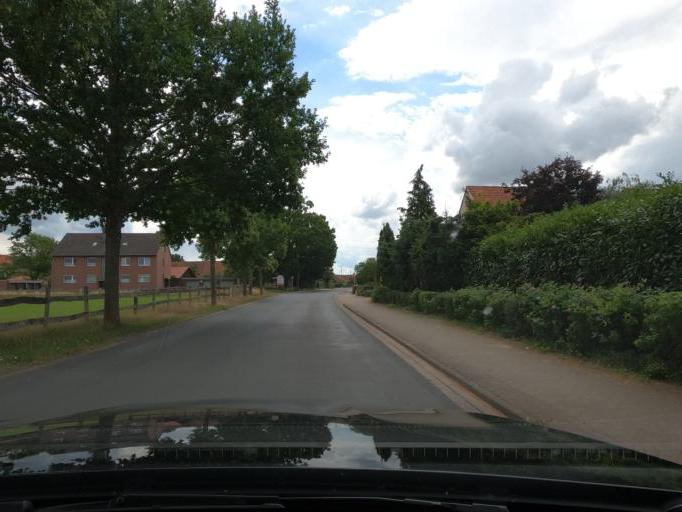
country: DE
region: Lower Saxony
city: Sehnde
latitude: 52.3420
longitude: 9.9108
